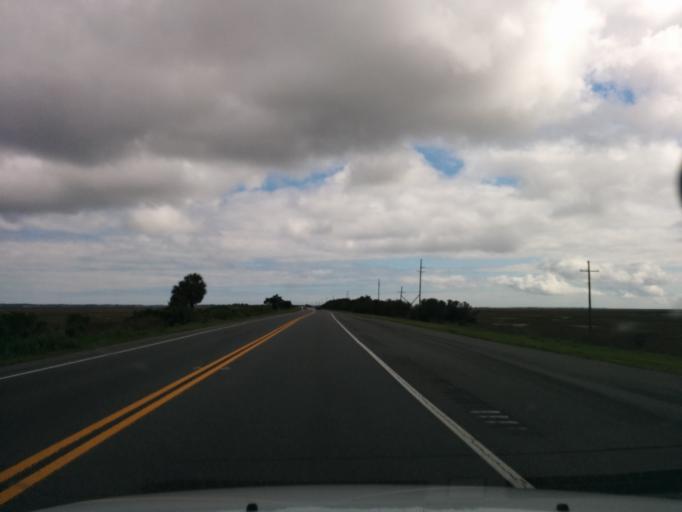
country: US
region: Georgia
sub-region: Glynn County
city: Brunswick
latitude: 31.0877
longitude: -81.4790
